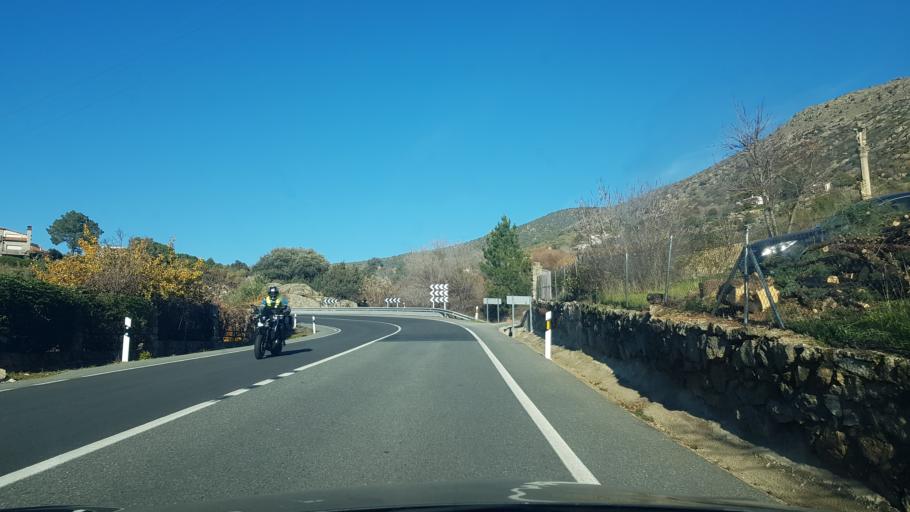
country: ES
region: Castille and Leon
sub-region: Provincia de Avila
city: El Tiemblo
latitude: 40.4350
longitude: -4.5525
